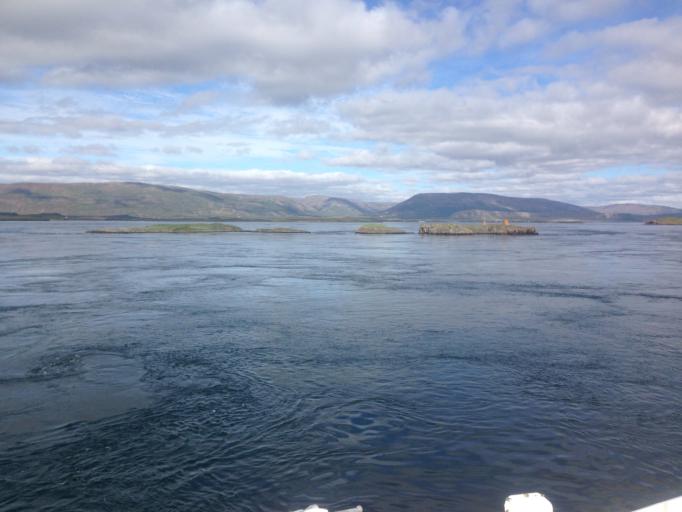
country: IS
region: West
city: Stykkisholmur
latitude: 65.1211
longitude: -22.4940
